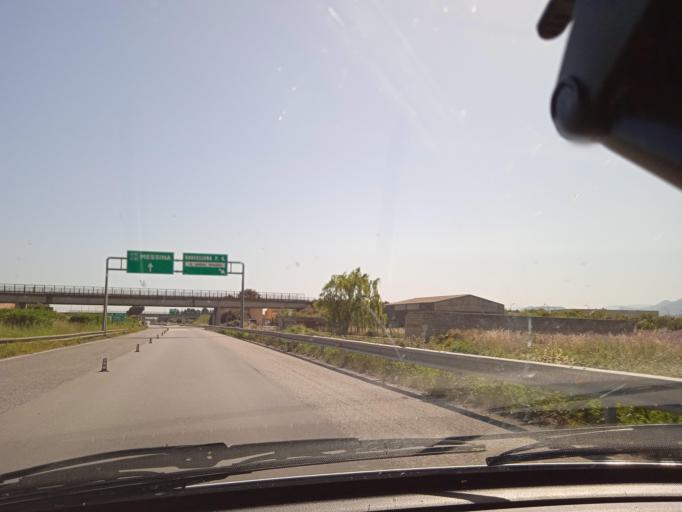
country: IT
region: Sicily
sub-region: Messina
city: Barcellona Pozzo di Gotto
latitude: 38.1539
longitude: 15.1838
